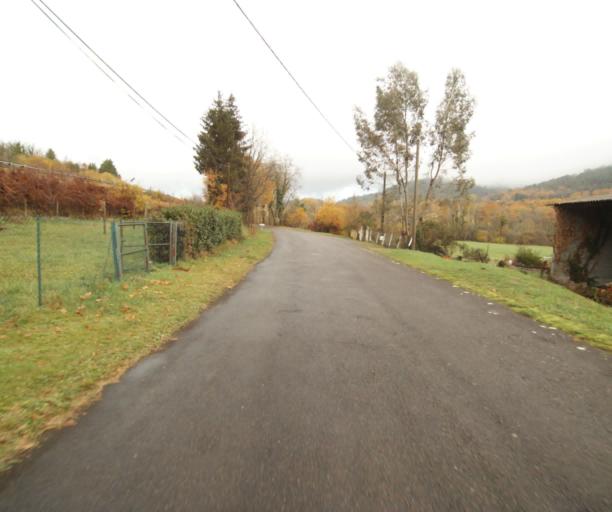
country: FR
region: Limousin
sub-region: Departement de la Correze
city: Cornil
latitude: 45.1827
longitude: 1.6574
